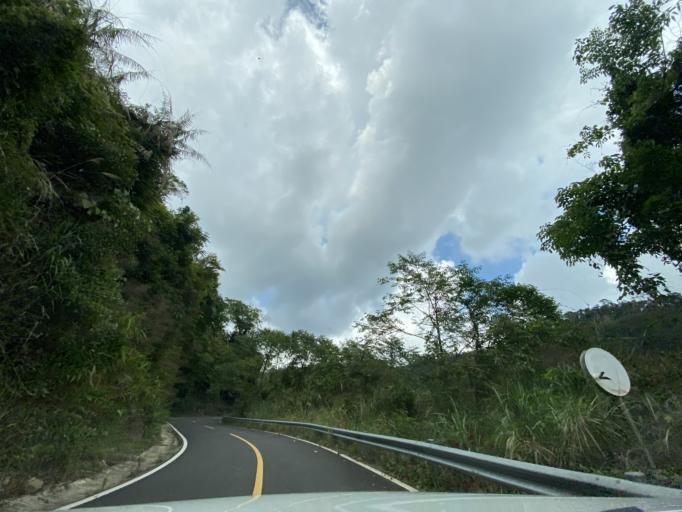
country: CN
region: Hainan
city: Benhao
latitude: 18.6896
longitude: 109.8796
